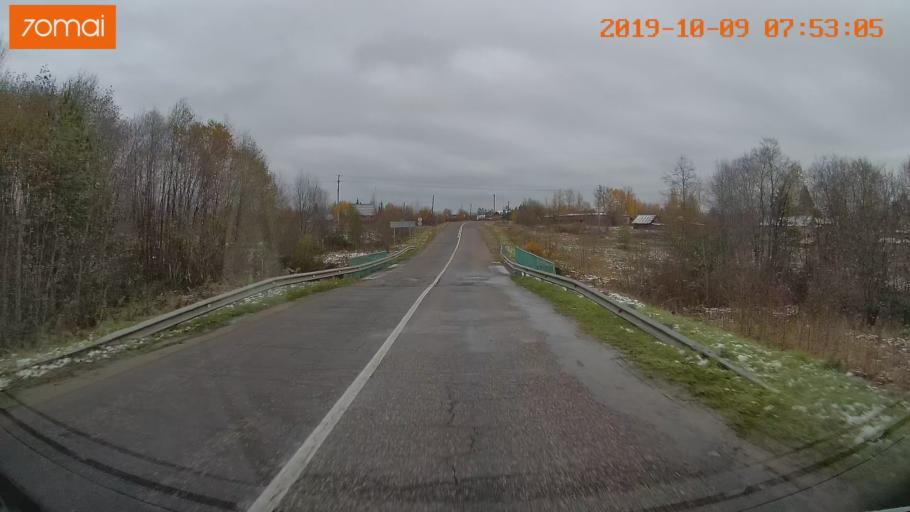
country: RU
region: Jaroslavl
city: Kukoboy
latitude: 58.6961
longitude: 39.8922
